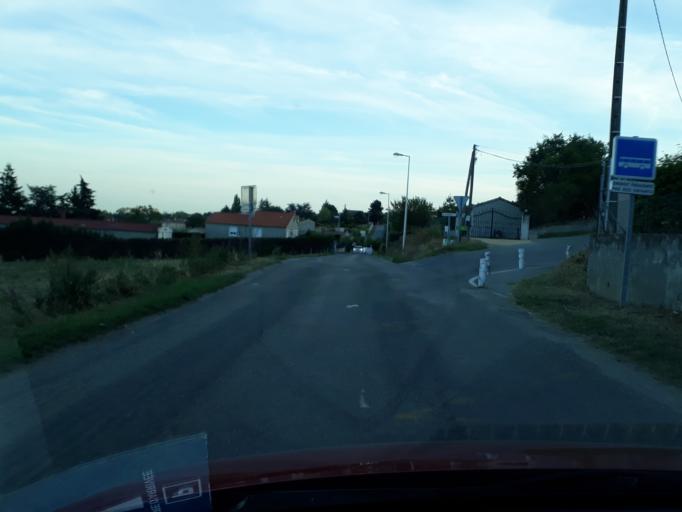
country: FR
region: Rhone-Alpes
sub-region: Departement de l'Ardeche
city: Felines
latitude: 45.3123
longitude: 4.7278
